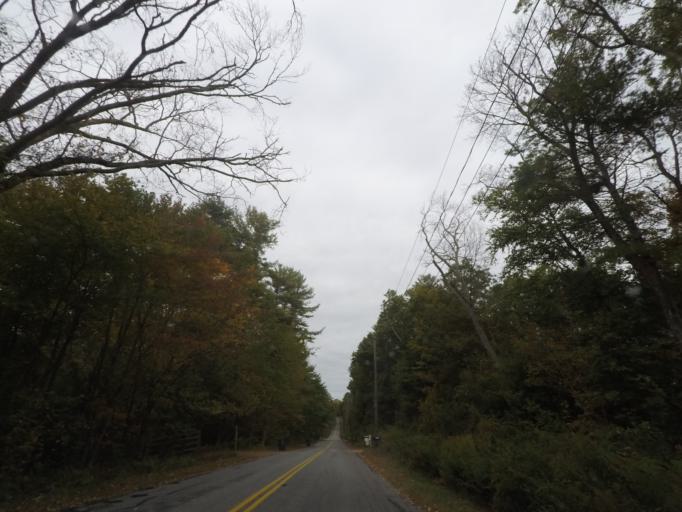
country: US
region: Connecticut
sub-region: Windham County
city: Thompson
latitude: 41.9437
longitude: -71.8336
